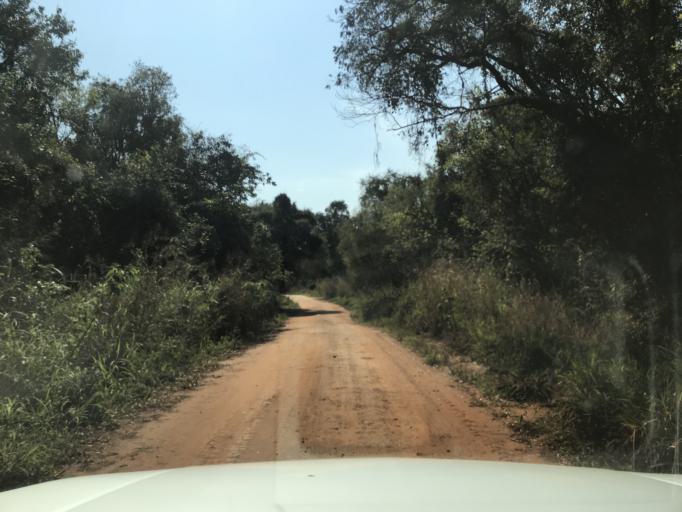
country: BR
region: Parana
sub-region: Palotina
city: Palotina
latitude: -24.2222
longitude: -53.7380
